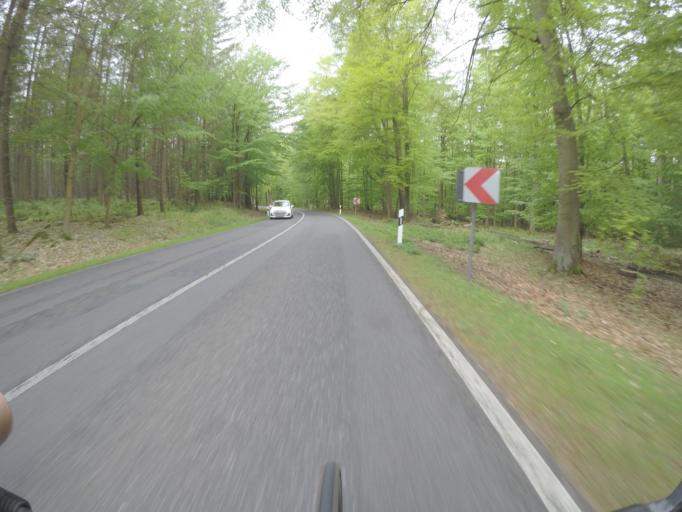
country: DE
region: Brandenburg
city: Joachimsthal
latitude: 52.9344
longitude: 13.7343
